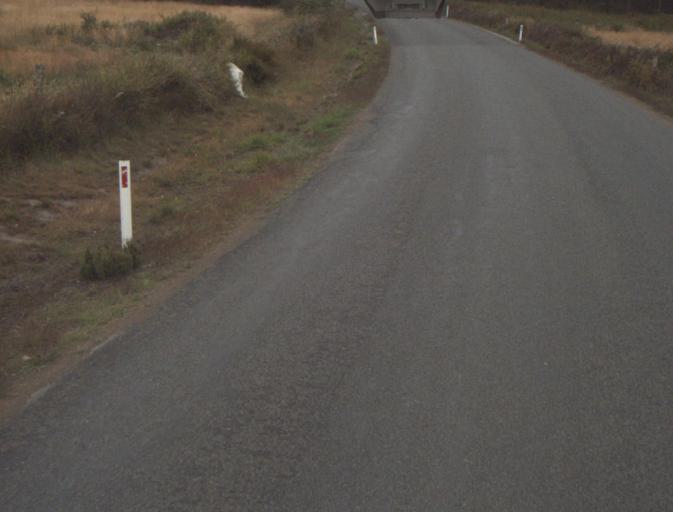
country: AU
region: Tasmania
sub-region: Launceston
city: Mayfield
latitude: -41.2370
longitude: 147.1823
